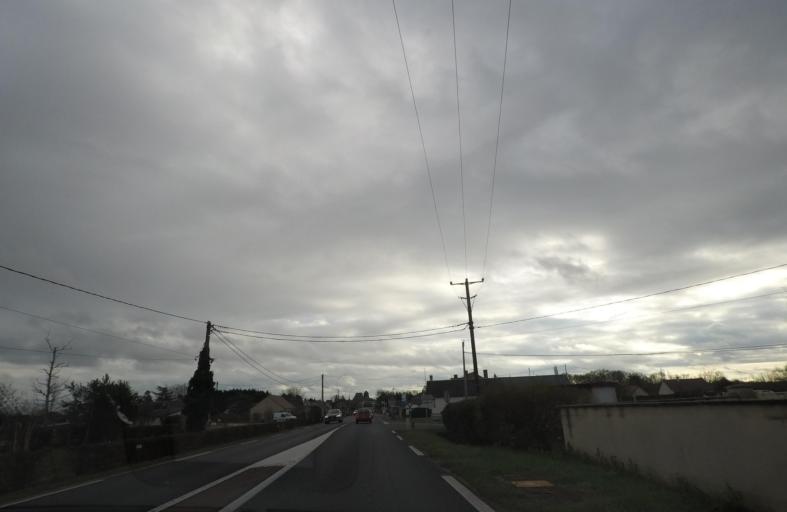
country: FR
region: Centre
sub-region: Departement du Loir-et-Cher
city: Mur-de-Sologne
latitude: 47.4146
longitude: 1.6020
